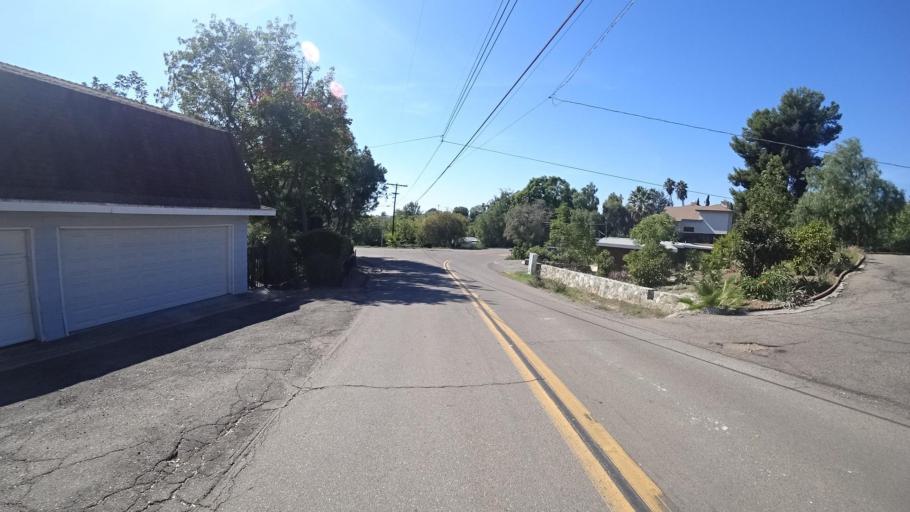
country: US
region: California
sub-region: San Diego County
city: Casa de Oro-Mount Helix
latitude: 32.7510
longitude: -116.9786
